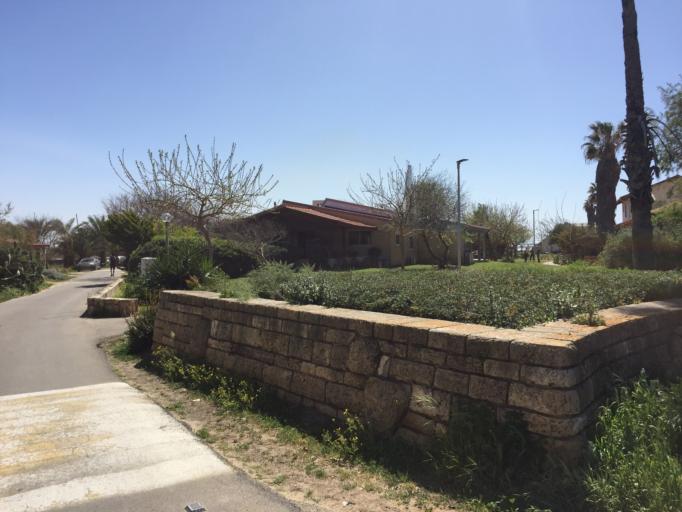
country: IL
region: Haifa
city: Qesarya
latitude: 32.4910
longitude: 34.8899
